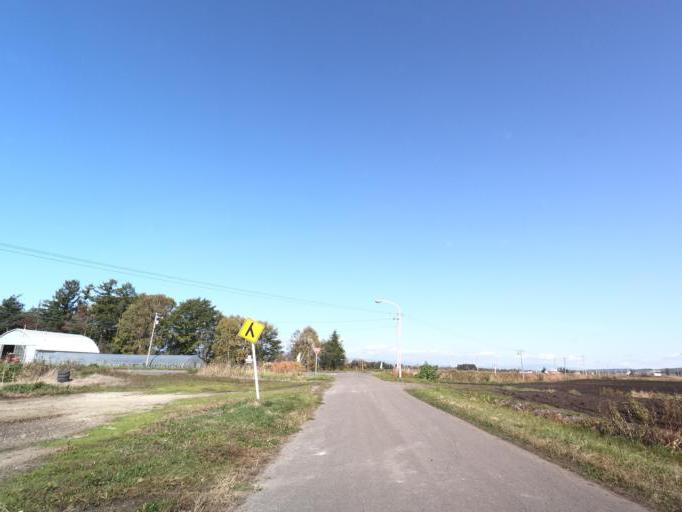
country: JP
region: Hokkaido
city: Otofuke
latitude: 43.0300
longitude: 143.2664
